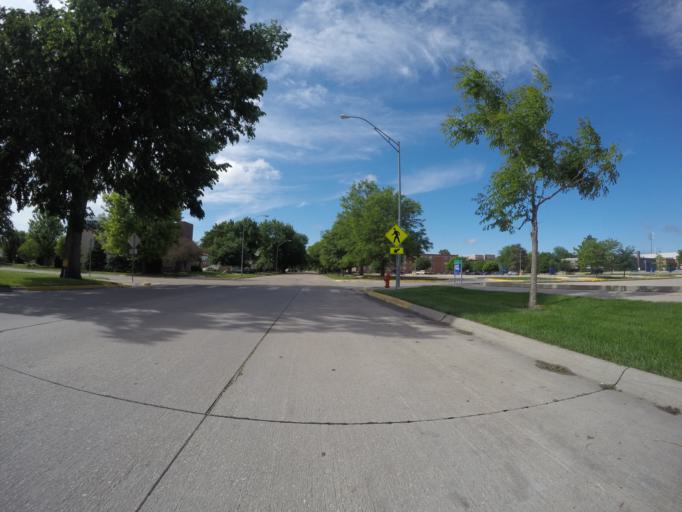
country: US
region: Nebraska
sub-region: Buffalo County
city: Kearney
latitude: 40.7039
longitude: -99.0939
